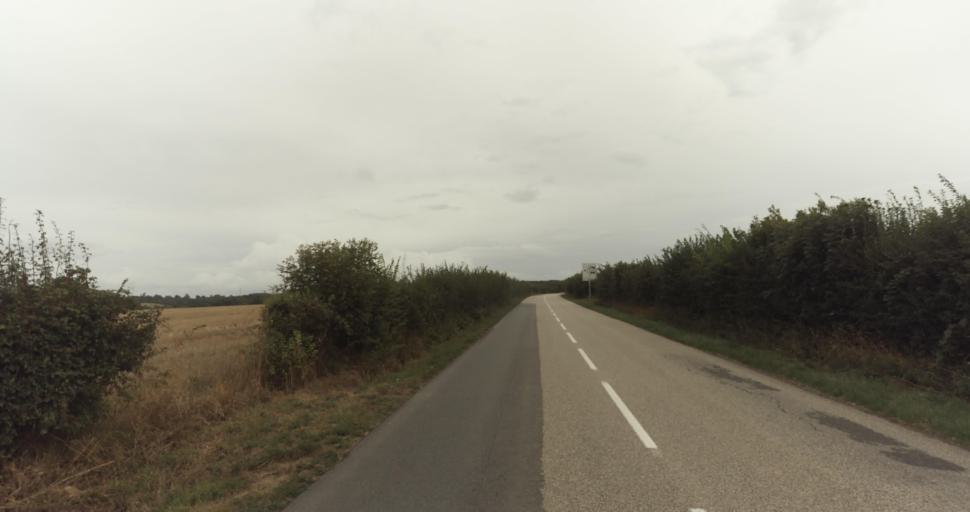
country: FR
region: Lower Normandy
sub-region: Departement de l'Orne
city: Gace
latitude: 48.8008
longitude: 0.3147
